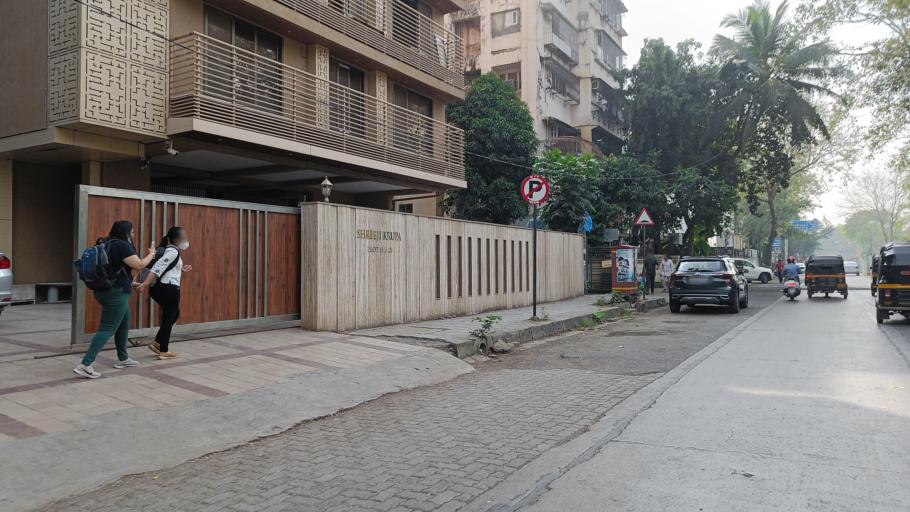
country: IN
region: Maharashtra
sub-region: Mumbai Suburban
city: Mumbai
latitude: 19.1049
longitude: 72.8369
